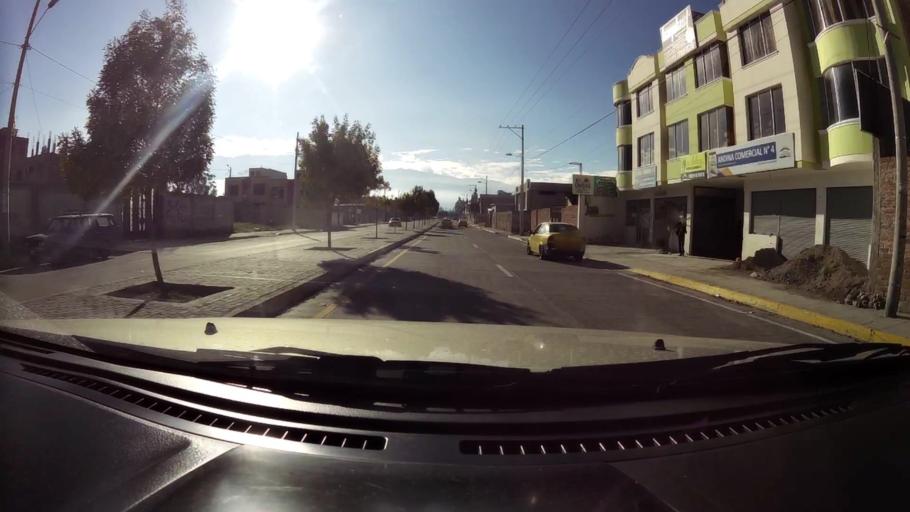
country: EC
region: Chimborazo
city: Riobamba
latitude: -1.6734
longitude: -78.6334
